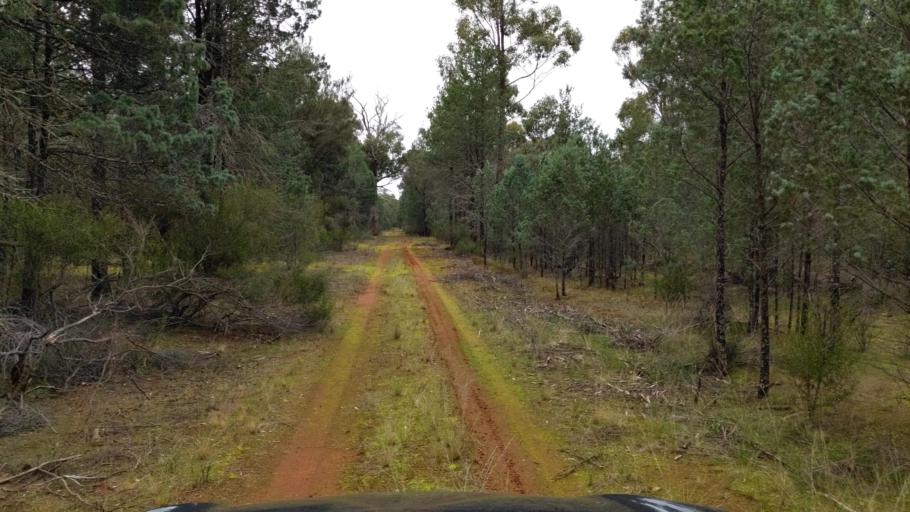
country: AU
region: New South Wales
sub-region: Coolamon
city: Coolamon
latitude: -34.8462
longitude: 146.9327
